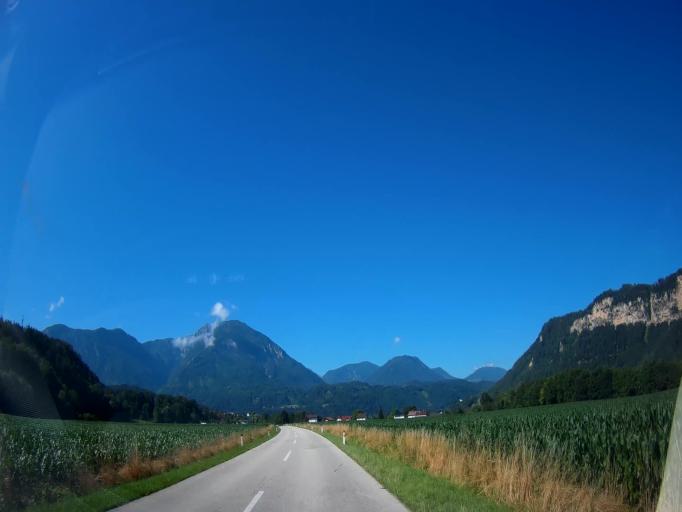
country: AT
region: Carinthia
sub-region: Politischer Bezirk Volkermarkt
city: Gallizien
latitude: 46.5846
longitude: 14.5137
